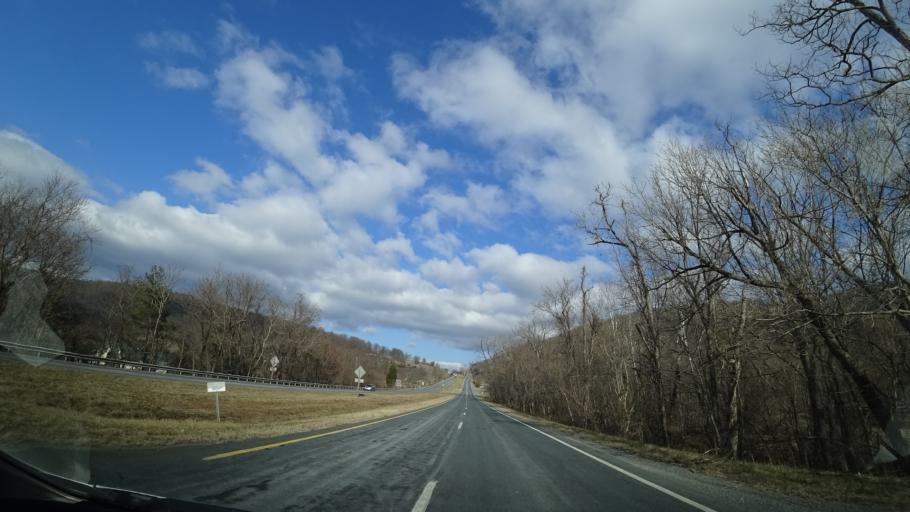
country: US
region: Virginia
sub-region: Warren County
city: Shenandoah Farms
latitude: 39.0080
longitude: -77.9526
